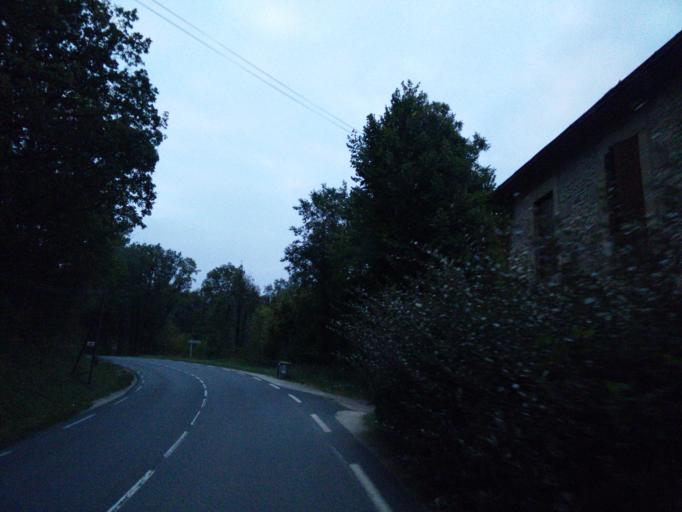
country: FR
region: Aquitaine
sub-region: Departement de la Dordogne
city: Sarlat-la-Caneda
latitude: 44.9074
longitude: 1.1875
